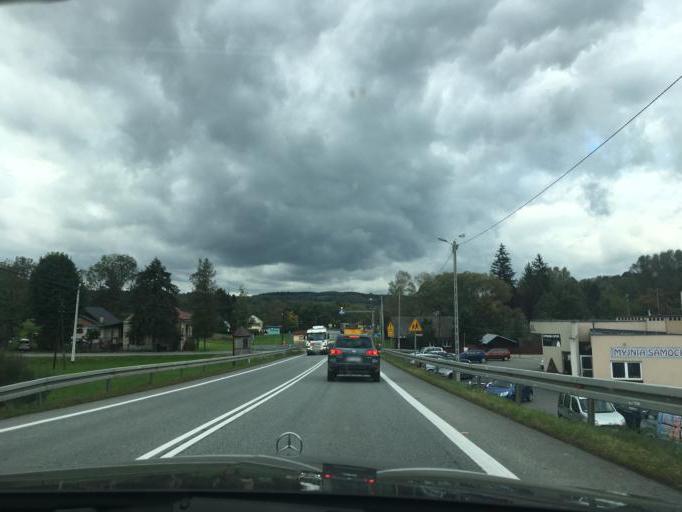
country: PL
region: Subcarpathian Voivodeship
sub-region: Powiat strzyzowski
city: Polomia
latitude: 49.8977
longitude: 21.8825
